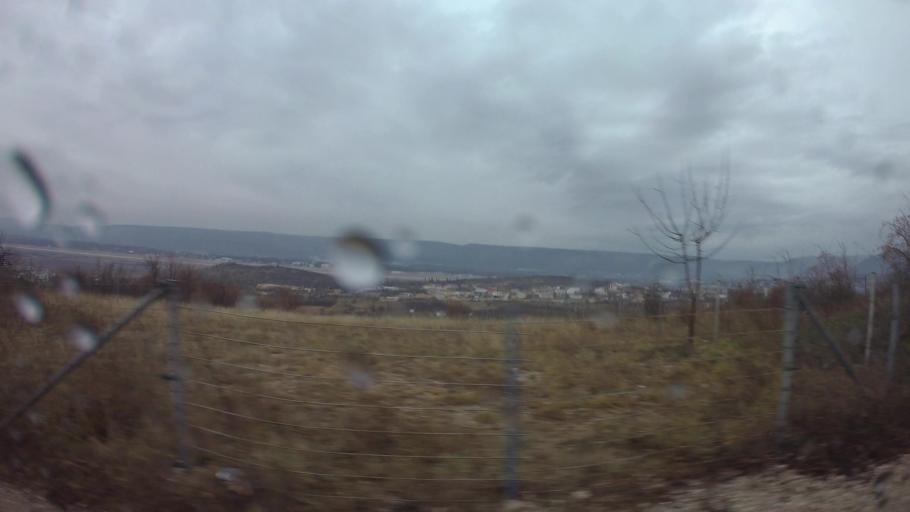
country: BA
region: Federation of Bosnia and Herzegovina
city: Blagaj
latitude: 43.2954
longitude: 17.8565
